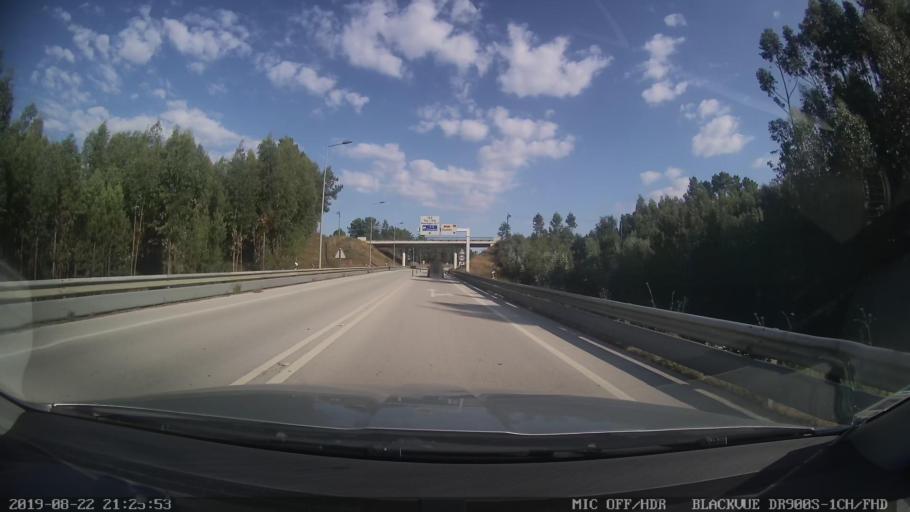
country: PT
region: Castelo Branco
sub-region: Serta
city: Serta
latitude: 39.8599
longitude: -8.1283
